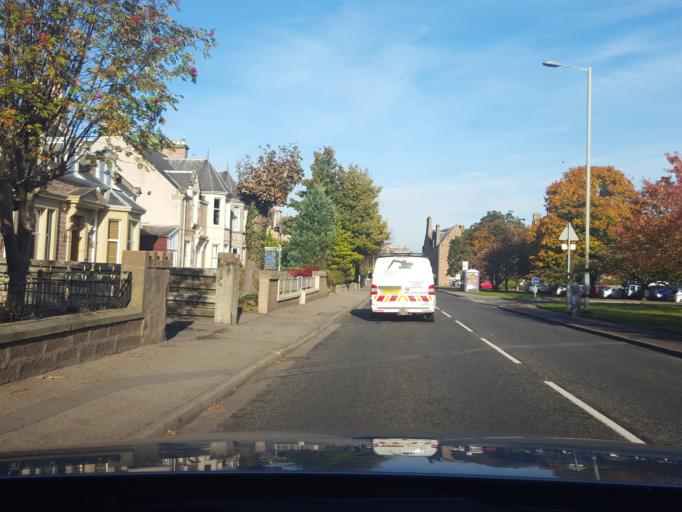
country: GB
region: Scotland
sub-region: Highland
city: Inverness
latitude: 57.4729
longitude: -4.2347
